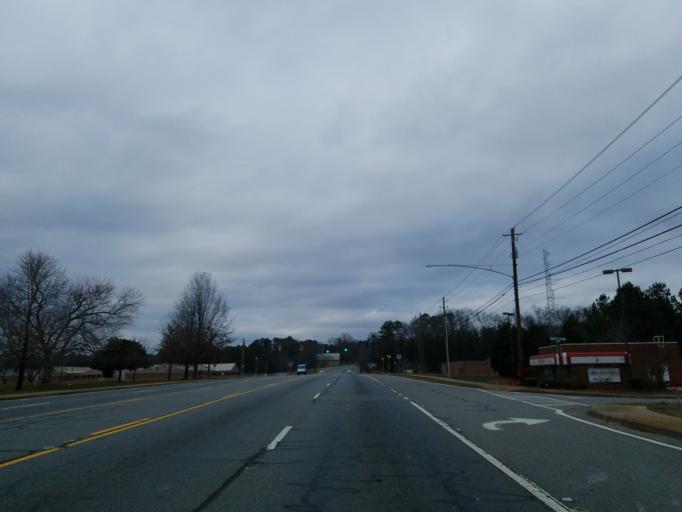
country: US
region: Georgia
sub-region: Cherokee County
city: Canton
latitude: 34.2335
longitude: -84.4999
